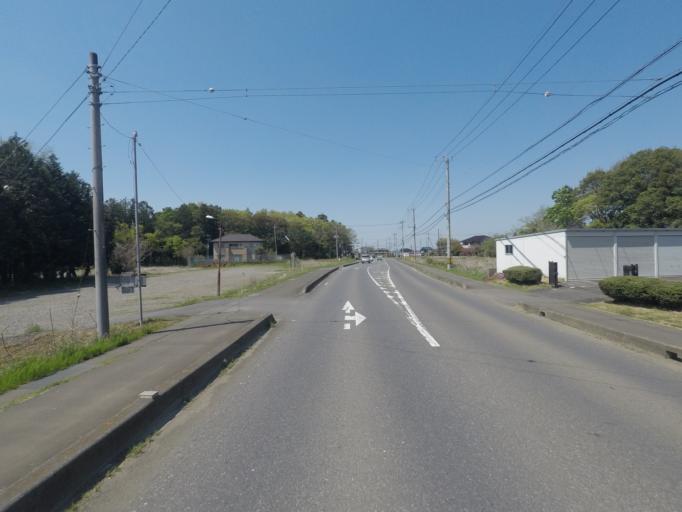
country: JP
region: Ibaraki
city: Ushiku
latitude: 35.9643
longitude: 140.1012
